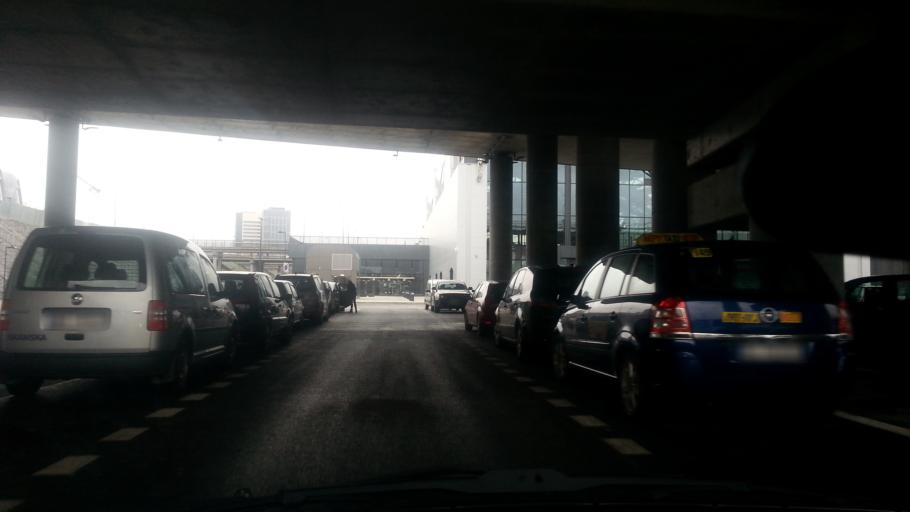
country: PL
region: Lodz Voivodeship
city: Lodz
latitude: 51.7691
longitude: 19.4733
